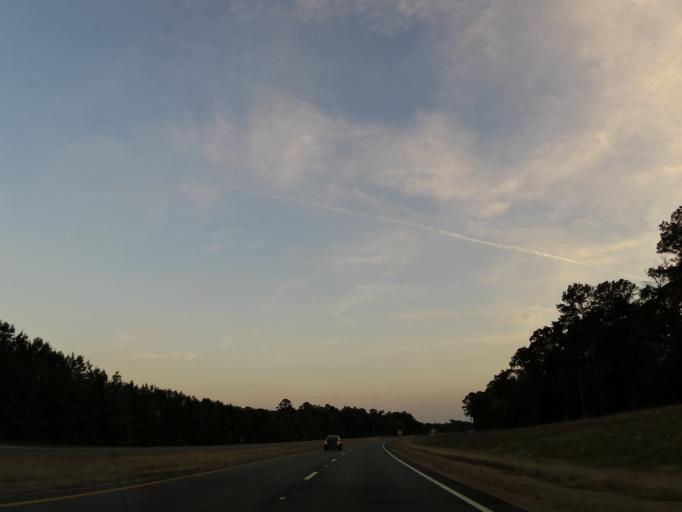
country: US
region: Mississippi
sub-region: Kemper County
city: De Kalb
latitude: 32.8057
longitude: -88.4546
